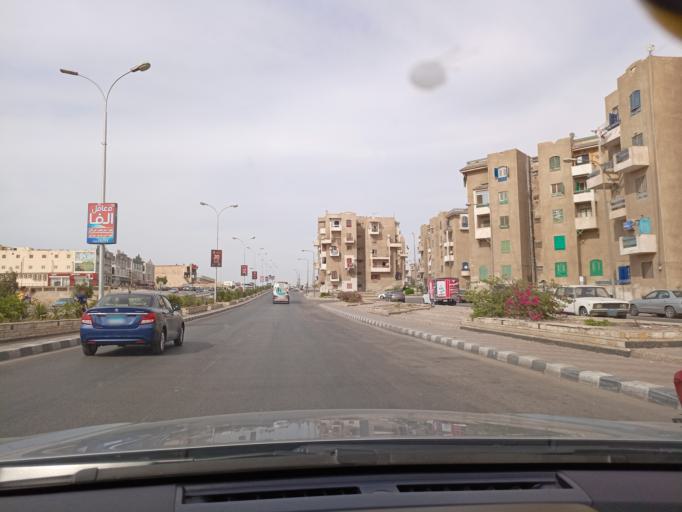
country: EG
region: Muhafazat al Qalyubiyah
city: Al Khankah
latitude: 30.2650
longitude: 31.4769
